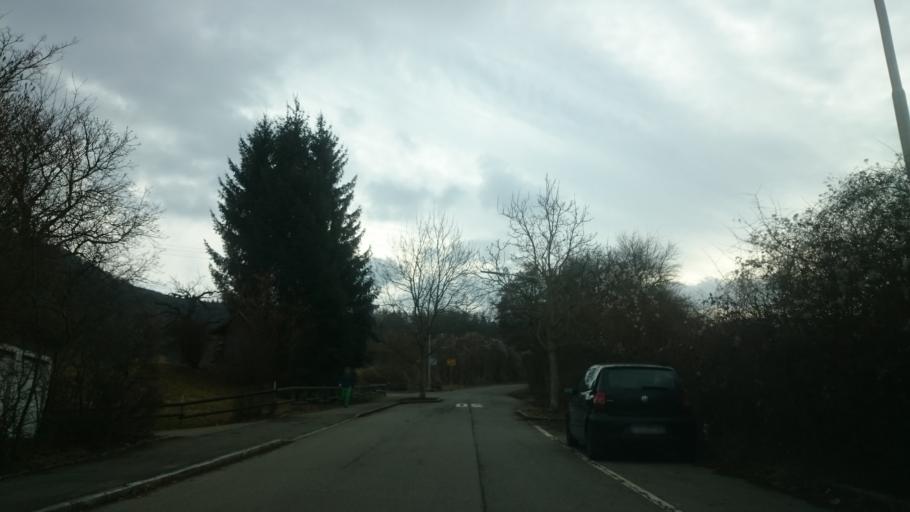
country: DE
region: Baden-Wuerttemberg
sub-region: Tuebingen Region
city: Mossingen
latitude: 48.3987
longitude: 9.0593
